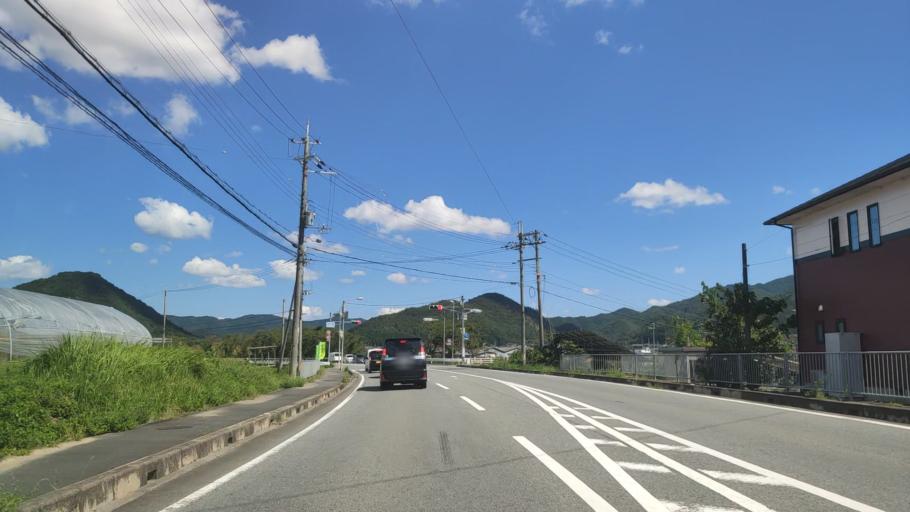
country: JP
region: Kyoto
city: Fukuchiyama
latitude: 35.1797
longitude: 135.1210
